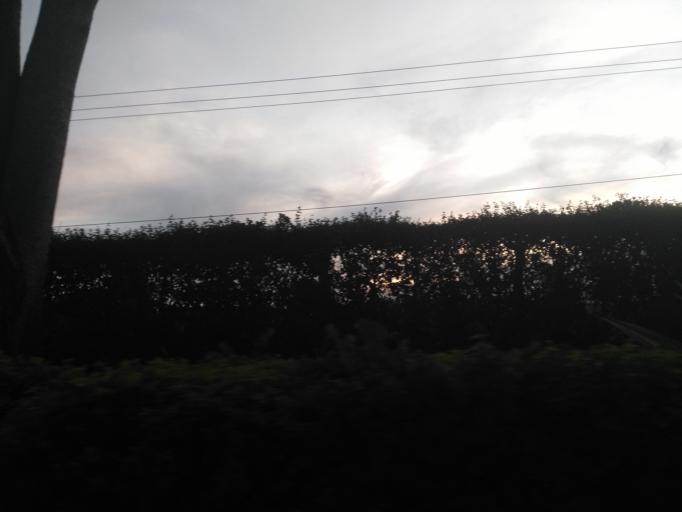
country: UG
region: Eastern Region
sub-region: Jinja District
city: Jinja
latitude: 0.4313
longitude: 33.1971
